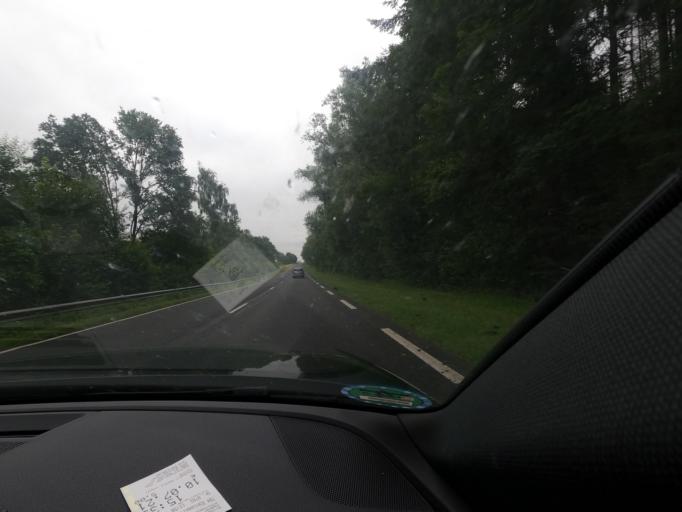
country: FR
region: Picardie
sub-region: Departement de la Somme
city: Moreuil
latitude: 49.7977
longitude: 2.5453
